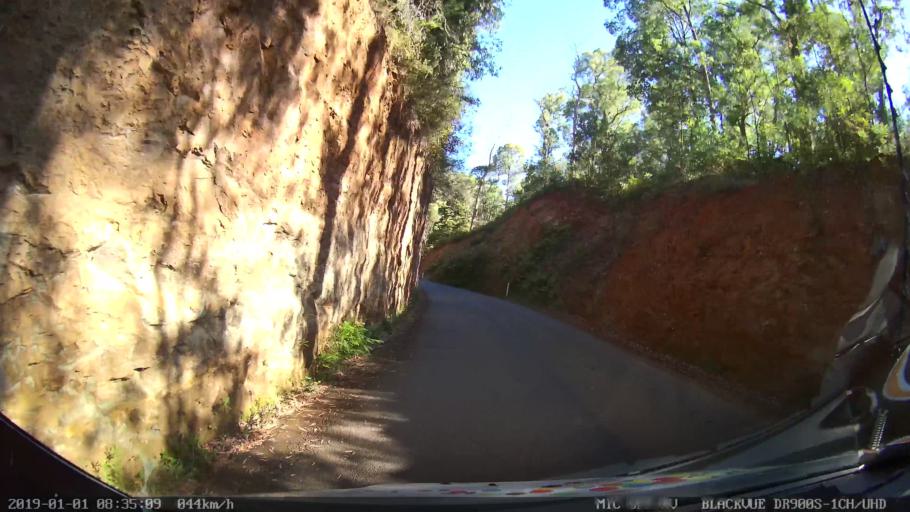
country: AU
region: New South Wales
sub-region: Snowy River
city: Jindabyne
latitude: -36.3507
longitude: 148.1933
